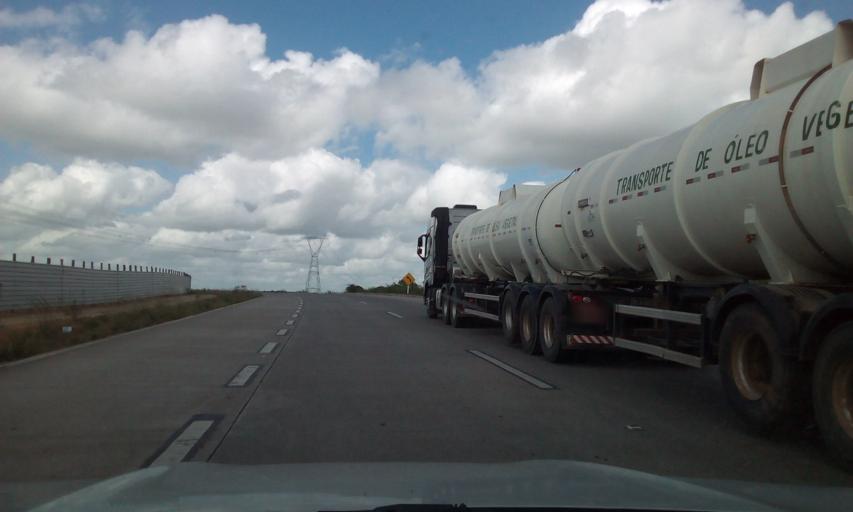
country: BR
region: Alagoas
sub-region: Messias
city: Messias
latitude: -9.4026
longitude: -35.8381
